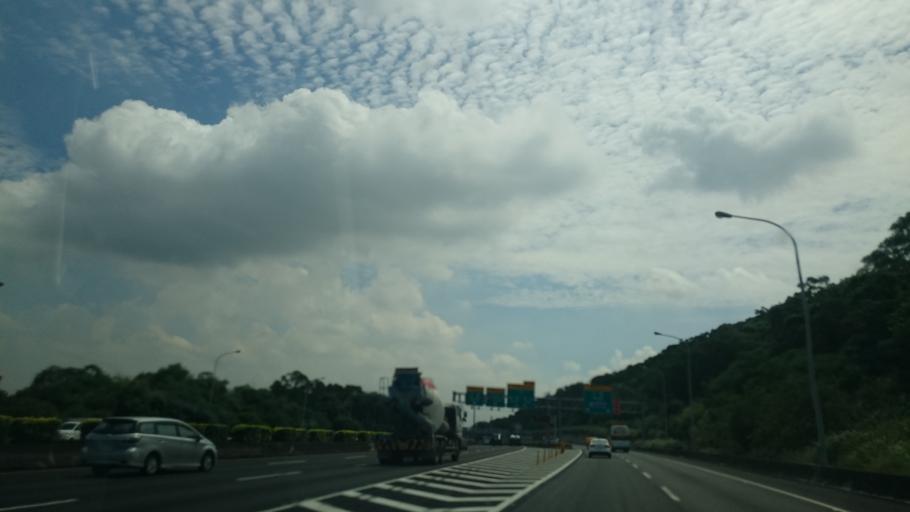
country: TW
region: Taiwan
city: Daxi
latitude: 24.9016
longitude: 121.1563
